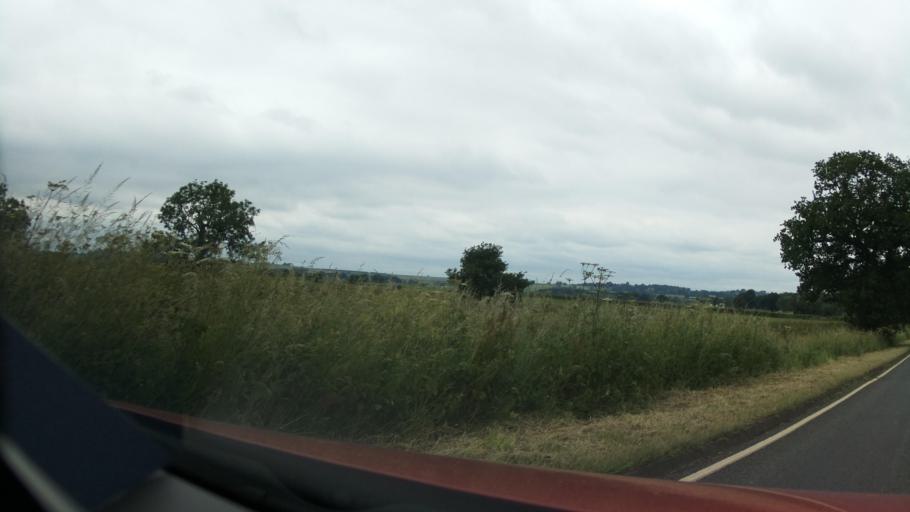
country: GB
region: England
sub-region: Leicestershire
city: Melton Mowbray
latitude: 52.7230
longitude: -0.8360
